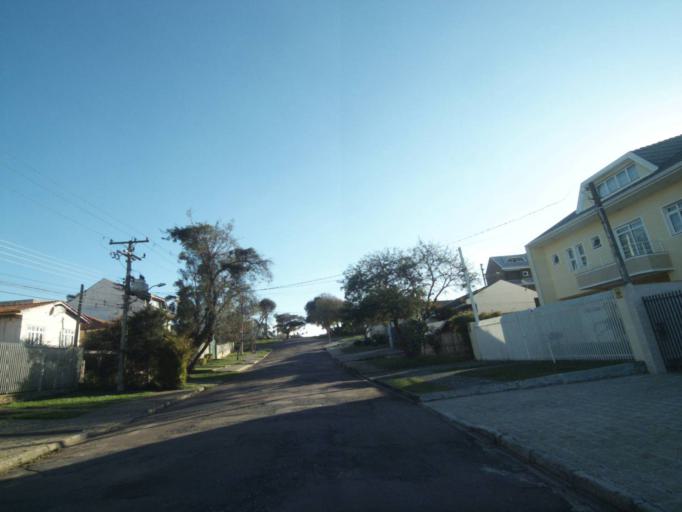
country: BR
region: Parana
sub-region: Curitiba
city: Curitiba
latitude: -25.3862
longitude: -49.2476
